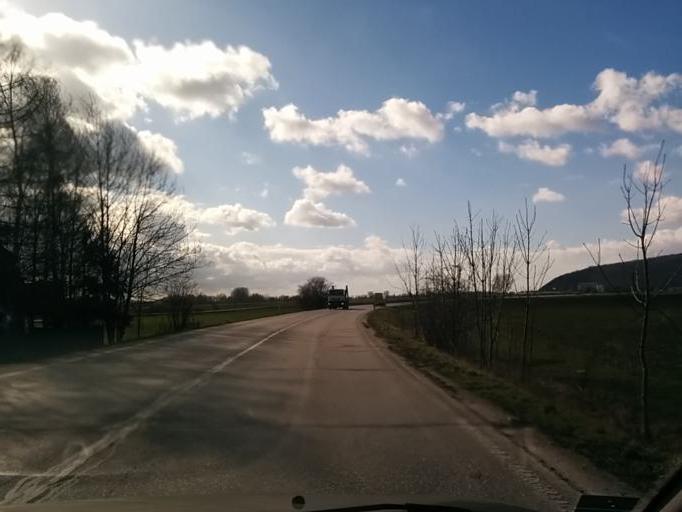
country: SK
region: Trenciansky
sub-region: Okres Nove Mesto nad Vahom
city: Nove Mesto nad Vahom
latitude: 48.8079
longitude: 17.8874
